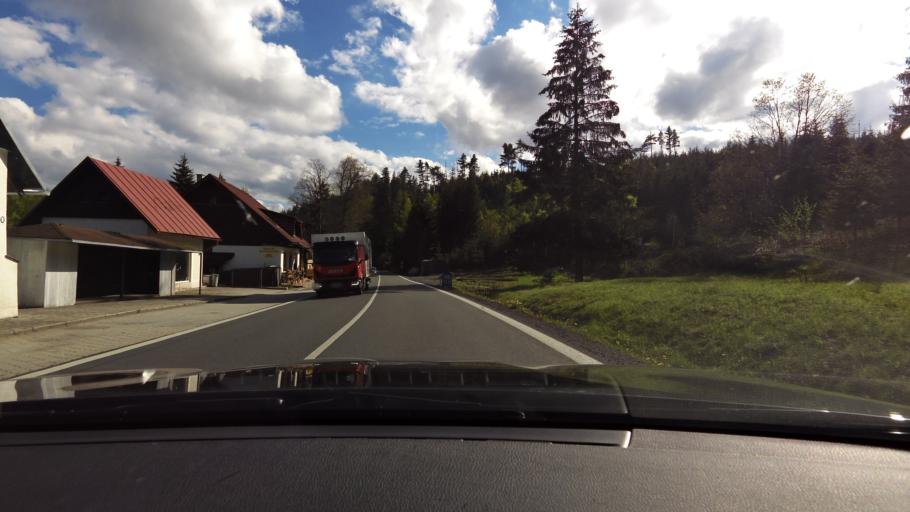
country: CZ
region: Plzensky
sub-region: Okres Klatovy
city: Zelezna Ruda
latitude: 49.1337
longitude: 13.2197
